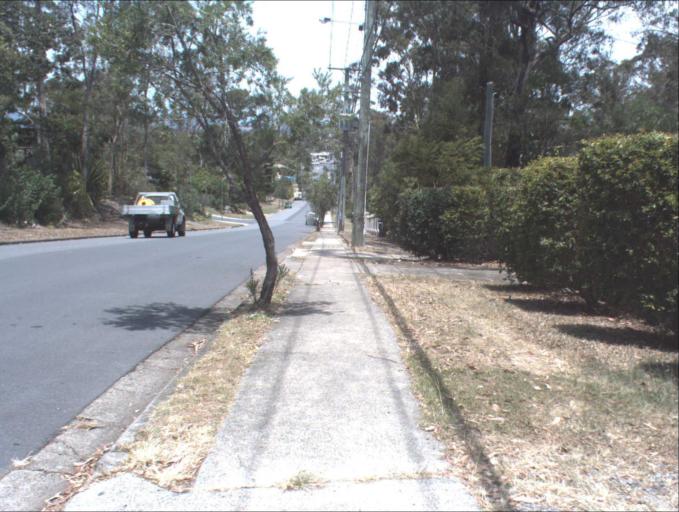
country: AU
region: Queensland
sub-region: Logan
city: Beenleigh
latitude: -27.6662
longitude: 153.1981
